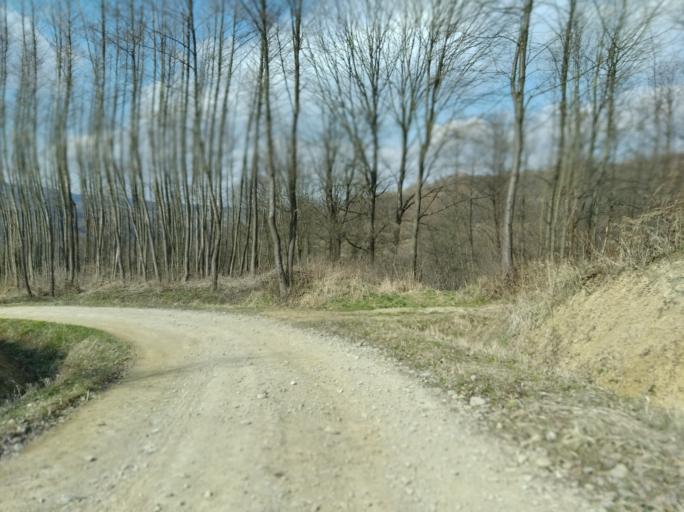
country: PL
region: Subcarpathian Voivodeship
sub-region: Powiat strzyzowski
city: Jawornik
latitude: 49.8214
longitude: 21.8471
